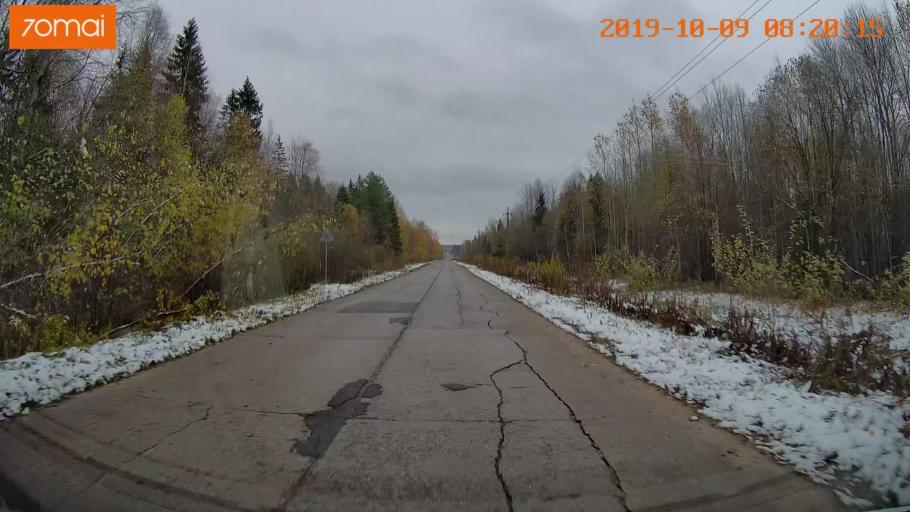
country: RU
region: Vologda
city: Gryazovets
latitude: 58.7429
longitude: 40.2564
